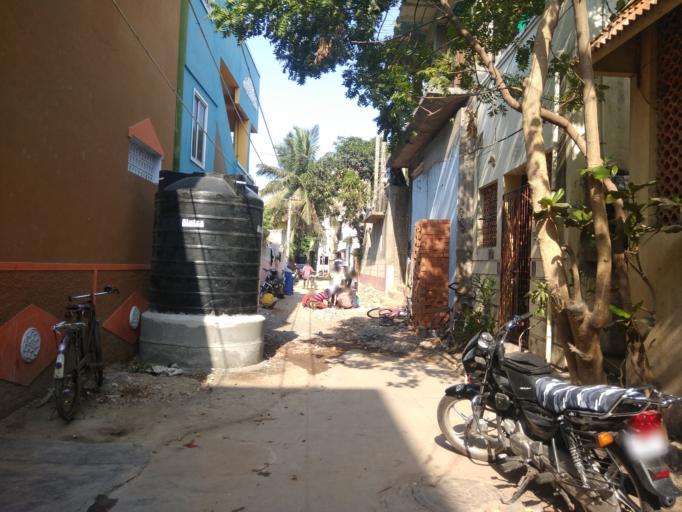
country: IN
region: Tamil Nadu
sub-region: Kancheepuram
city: Perungudi
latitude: 12.9805
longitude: 80.2386
